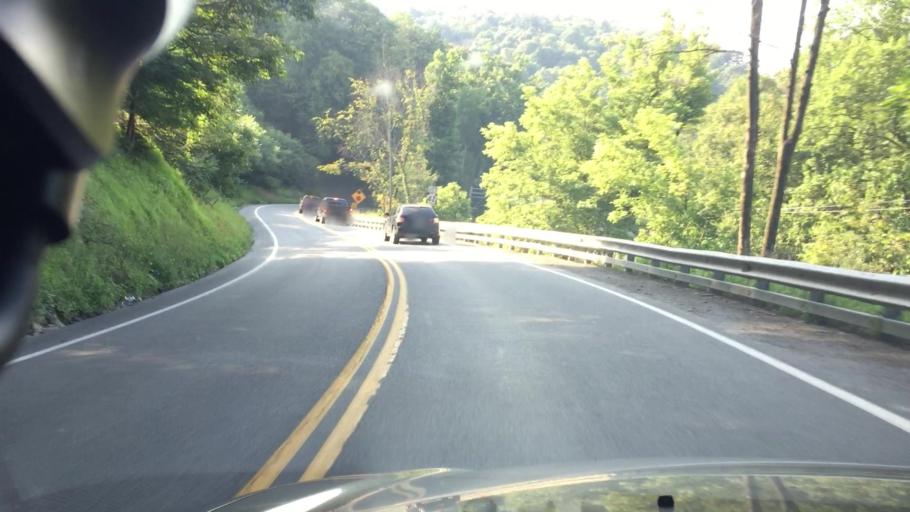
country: US
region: Pennsylvania
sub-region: Columbia County
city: Catawissa
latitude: 40.9404
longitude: -76.4558
